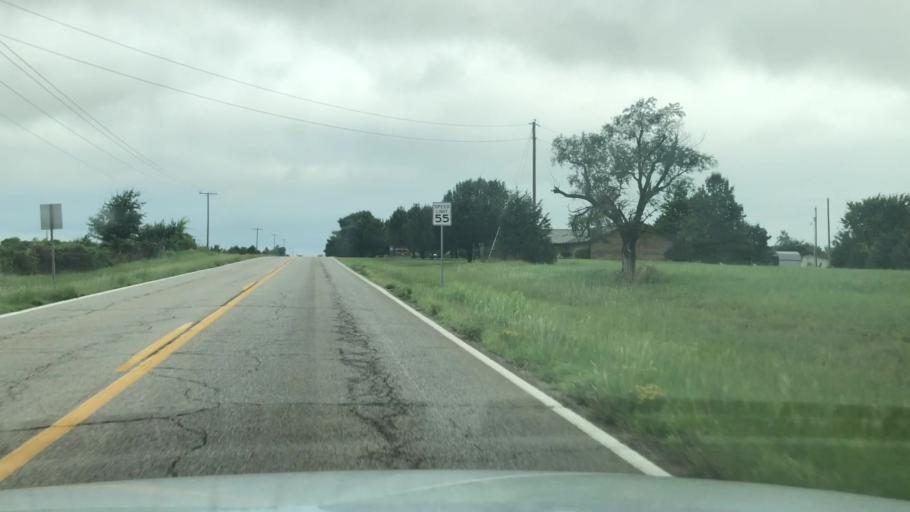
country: US
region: Oklahoma
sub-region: Nowata County
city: Nowata
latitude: 36.7085
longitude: -95.6564
